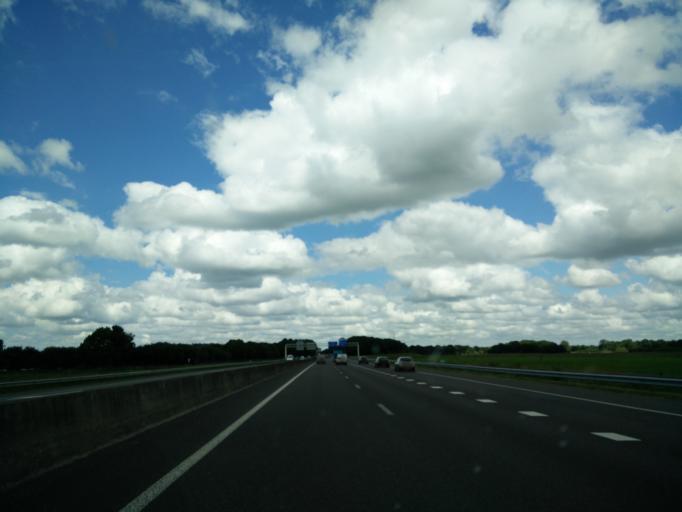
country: NL
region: Drenthe
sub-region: Gemeente Tynaarlo
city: Tynaarlo
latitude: 53.1181
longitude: 6.6107
